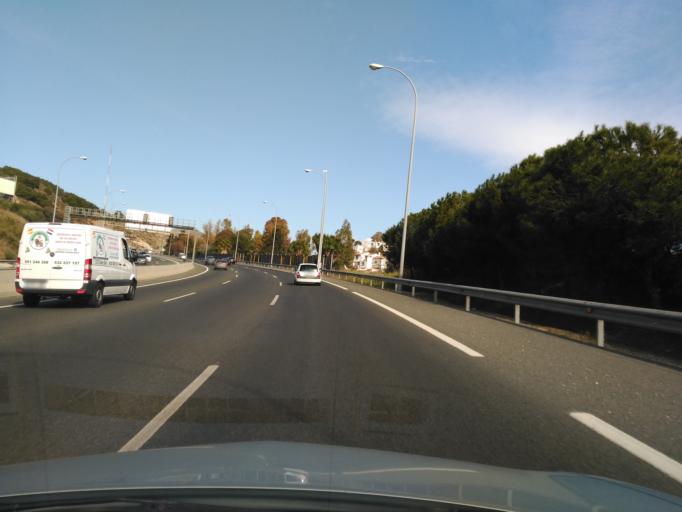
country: ES
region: Andalusia
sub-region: Provincia de Malaga
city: Malaga
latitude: 36.7263
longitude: -4.4535
